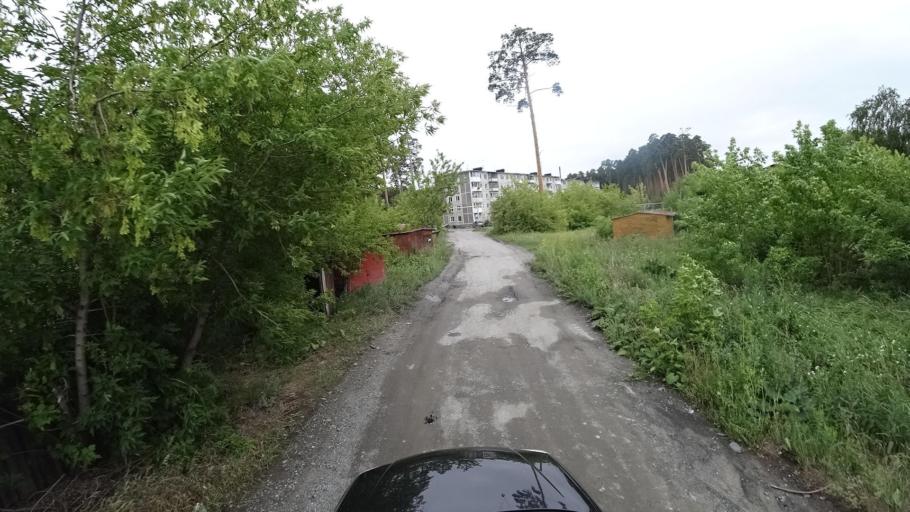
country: RU
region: Sverdlovsk
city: Kamyshlov
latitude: 56.8412
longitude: 62.7430
